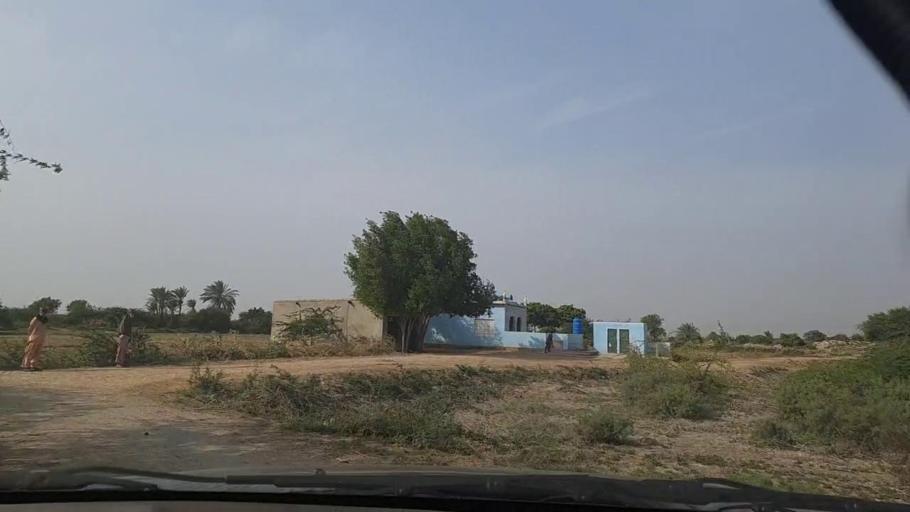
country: PK
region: Sindh
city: Thatta
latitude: 24.6172
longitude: 67.9512
